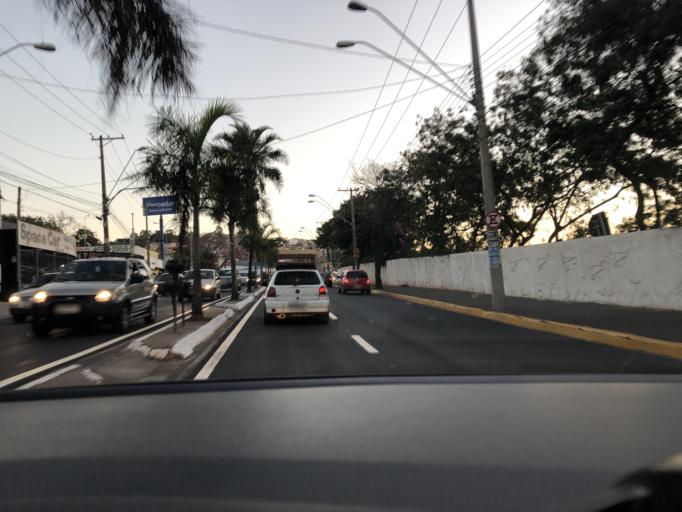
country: BR
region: Sao Paulo
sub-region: Varzea Paulista
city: Varzea Paulista
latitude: -23.2119
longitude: -46.8320
